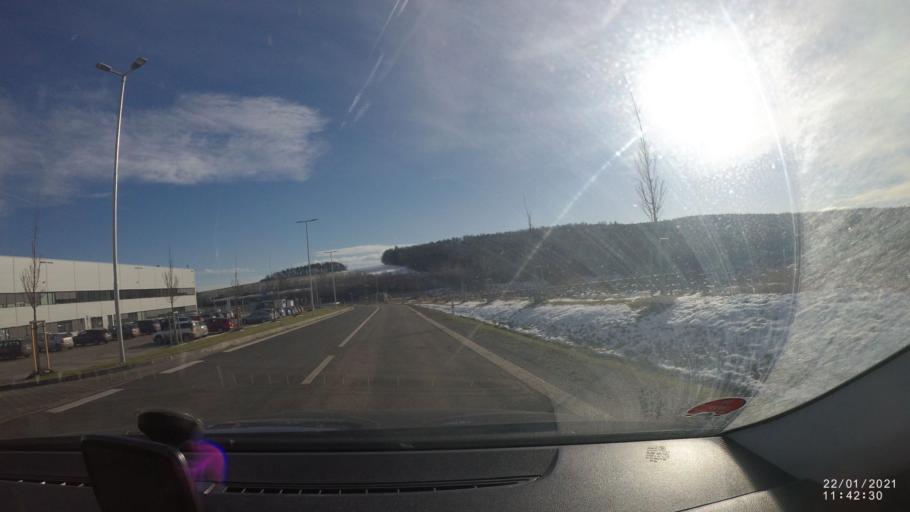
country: CZ
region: Plzensky
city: Zbiroh
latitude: 49.8409
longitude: 13.8111
